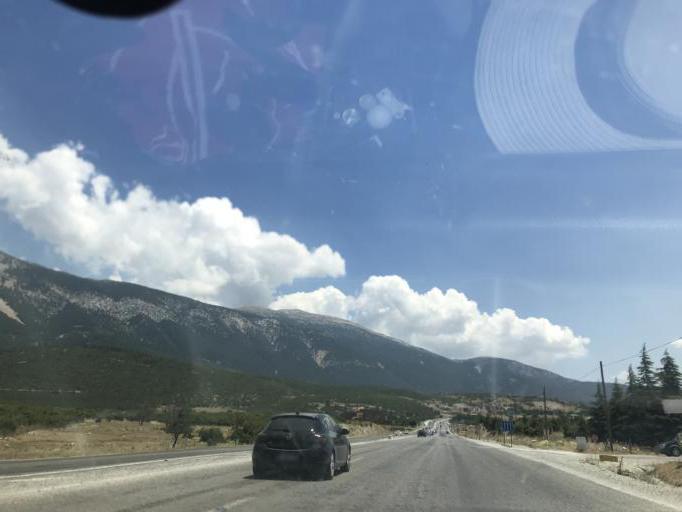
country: TR
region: Denizli
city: Honaz
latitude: 37.6966
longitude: 29.2049
